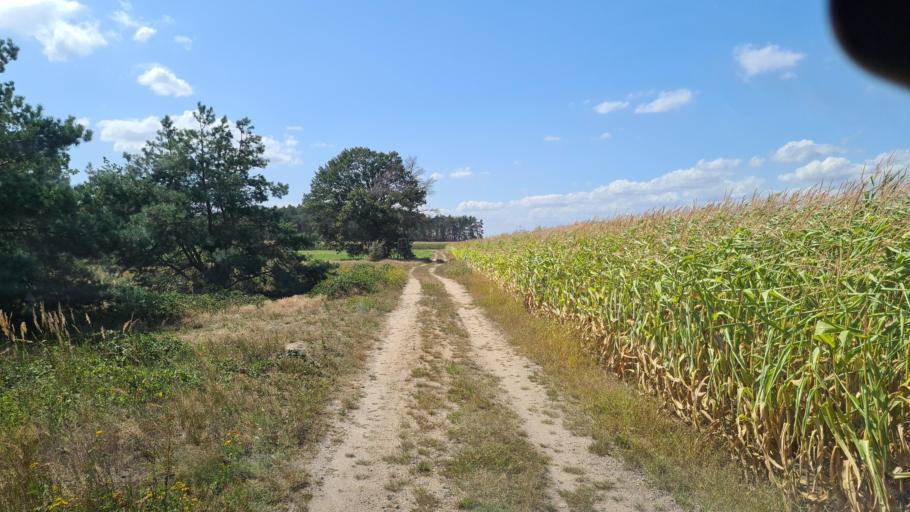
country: DE
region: Brandenburg
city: Schonborn
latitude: 51.5547
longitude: 13.4950
